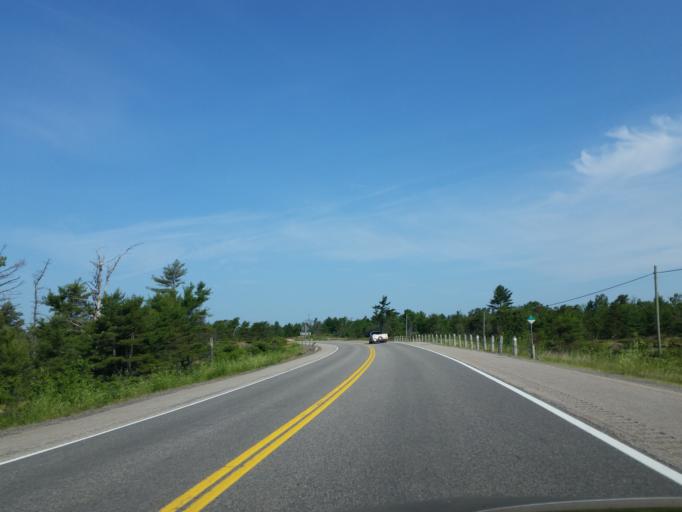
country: CA
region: Ontario
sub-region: Parry Sound District
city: Parry Sound
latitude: 45.7781
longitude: -80.4997
